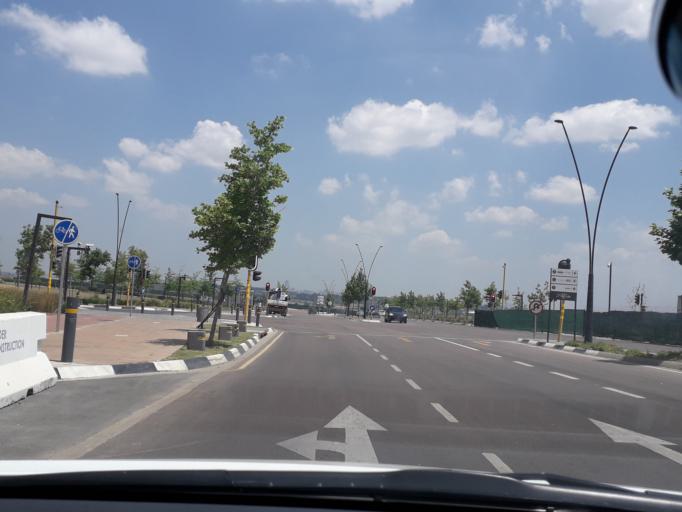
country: ZA
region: Gauteng
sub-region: City of Johannesburg Metropolitan Municipality
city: Midrand
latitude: -26.0141
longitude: 28.1048
